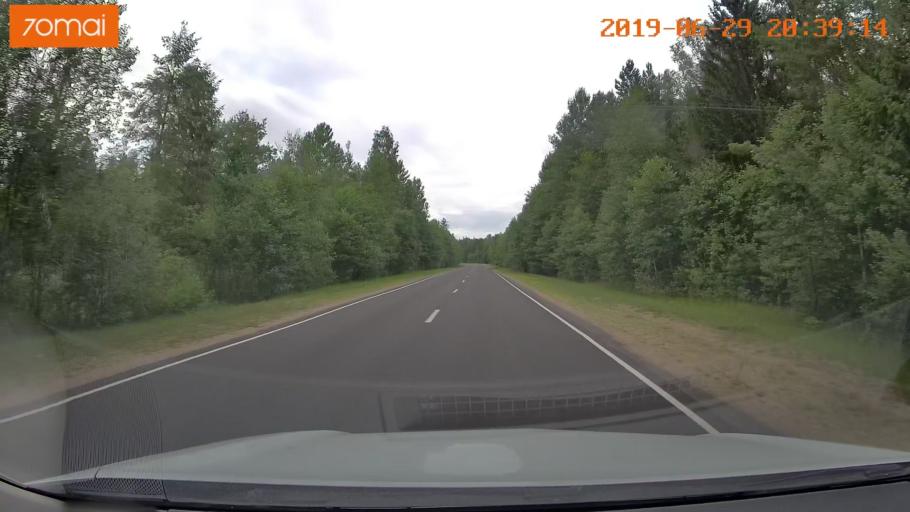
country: BY
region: Brest
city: Hantsavichy
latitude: 52.5598
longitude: 26.3632
